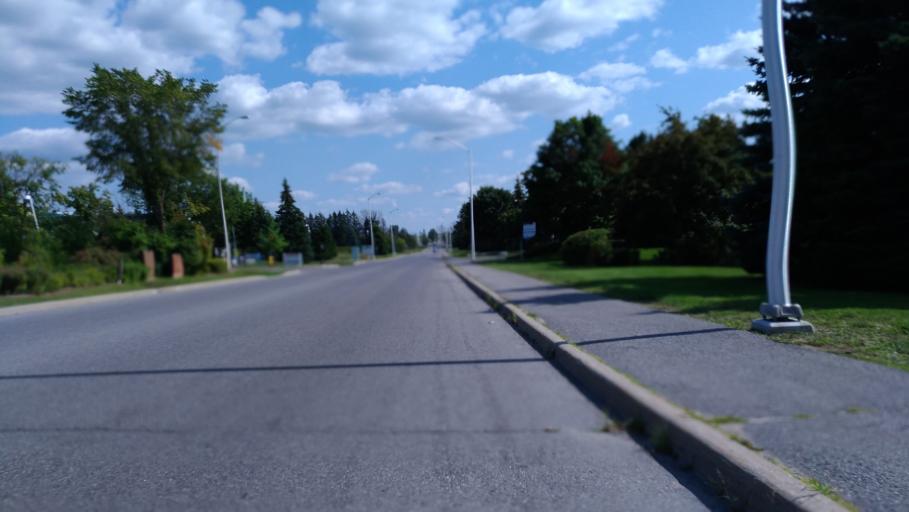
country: CA
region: Ontario
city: Bells Corners
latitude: 45.3449
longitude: -75.9234
